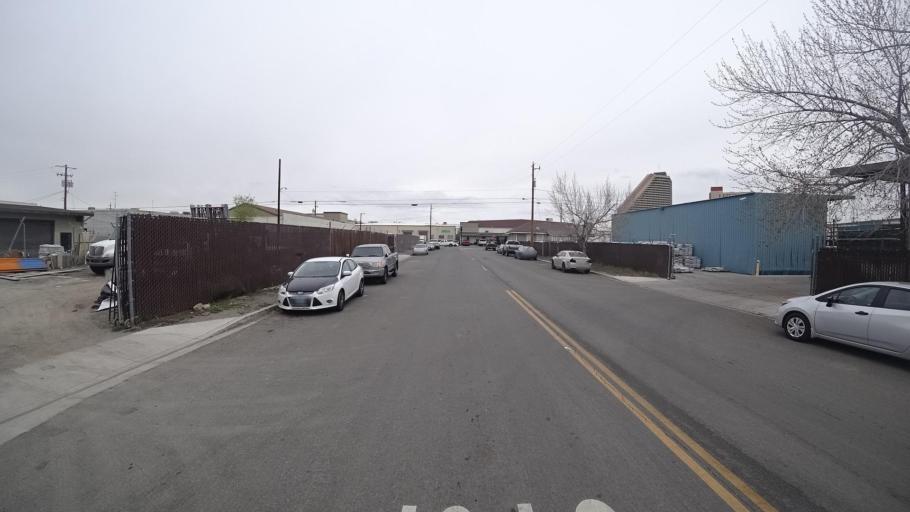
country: US
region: Nevada
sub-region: Washoe County
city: Sparks
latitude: 39.5296
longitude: -119.7631
